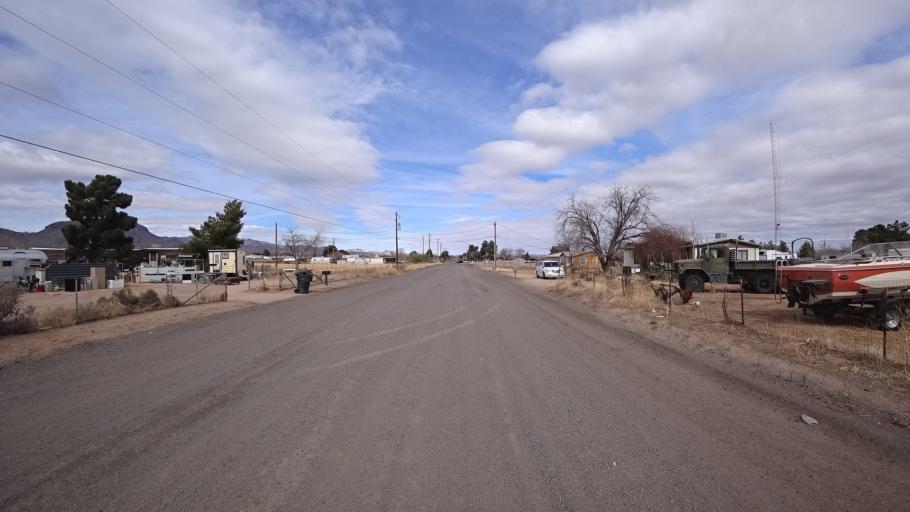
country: US
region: Arizona
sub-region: Mohave County
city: New Kingman-Butler
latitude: 35.2377
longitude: -114.0200
